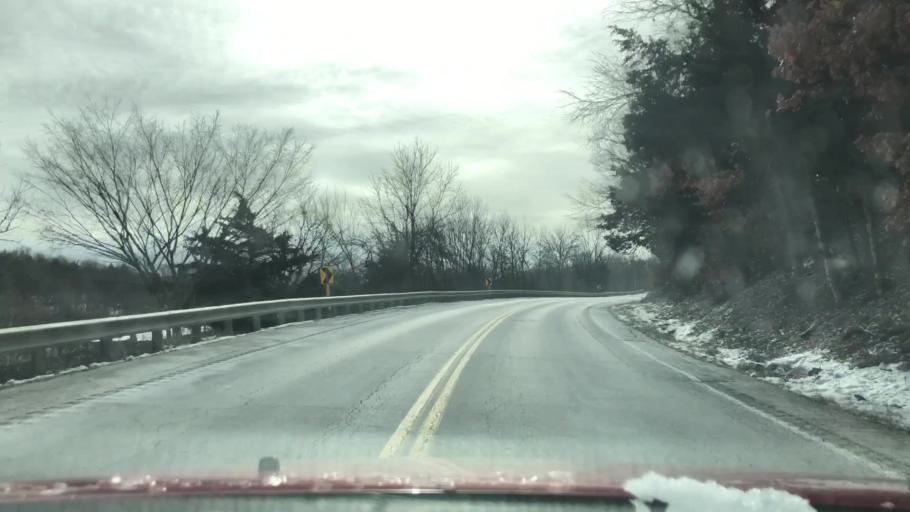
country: US
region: Missouri
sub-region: Jackson County
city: Oak Grove
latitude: 38.9386
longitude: -94.1327
